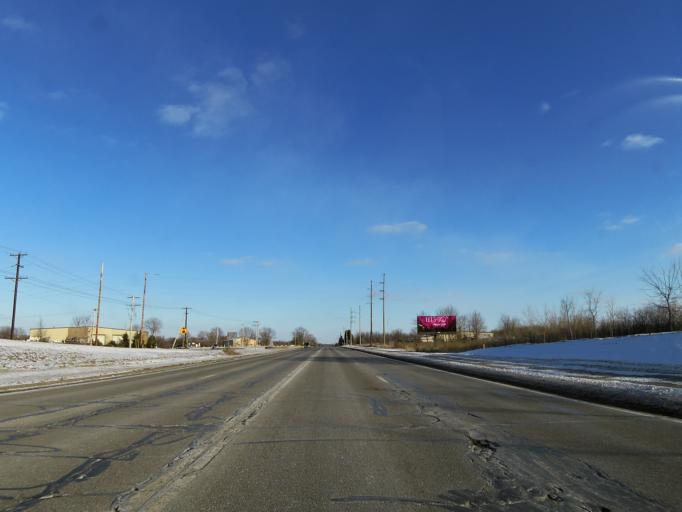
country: US
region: Minnesota
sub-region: Scott County
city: Prior Lake
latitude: 44.7037
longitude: -93.4025
